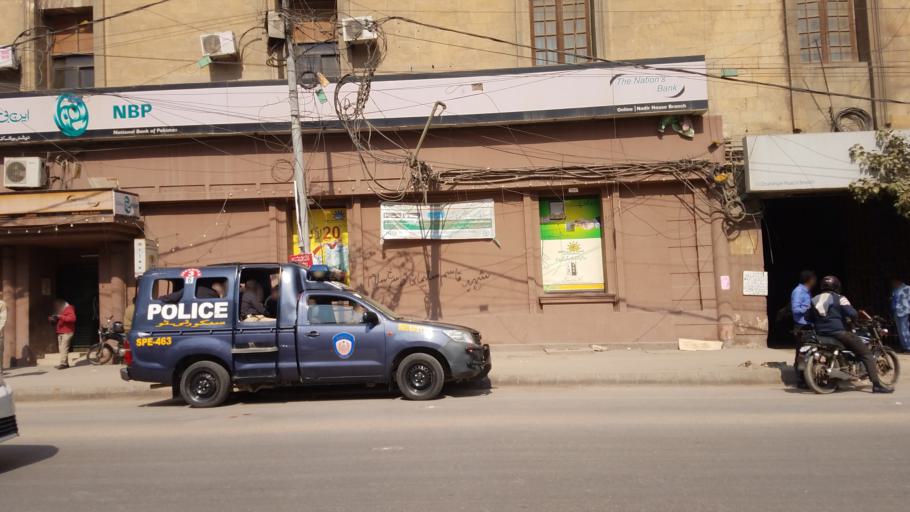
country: PK
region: Sindh
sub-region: Karachi District
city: Karachi
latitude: 24.8492
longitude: 67.0010
